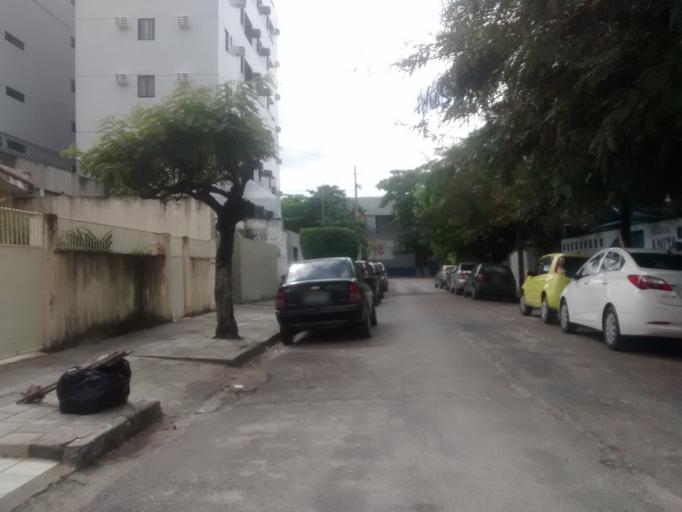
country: BR
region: Pernambuco
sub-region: Recife
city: Recife
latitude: -8.0952
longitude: -34.9125
